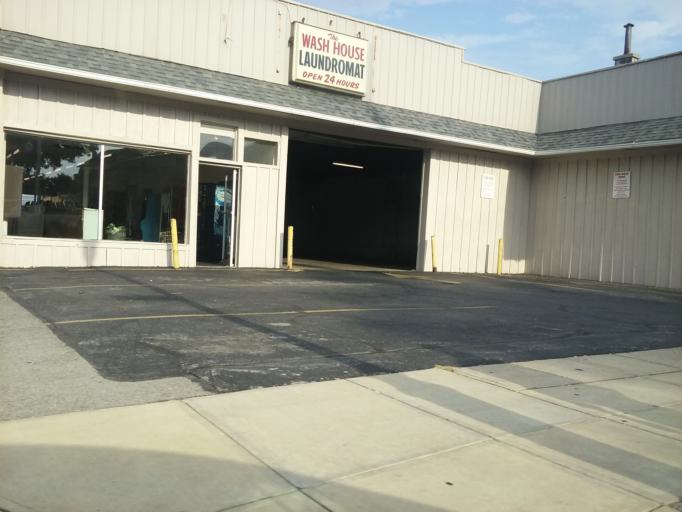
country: US
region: Ohio
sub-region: Wood County
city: Bowling Green
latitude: 41.3768
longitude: -83.6503
